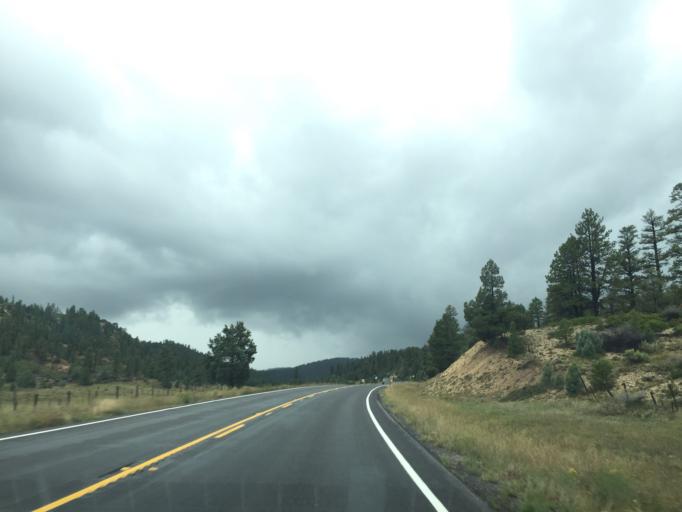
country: US
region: Utah
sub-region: Garfield County
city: Panguitch
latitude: 37.4625
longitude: -112.5197
